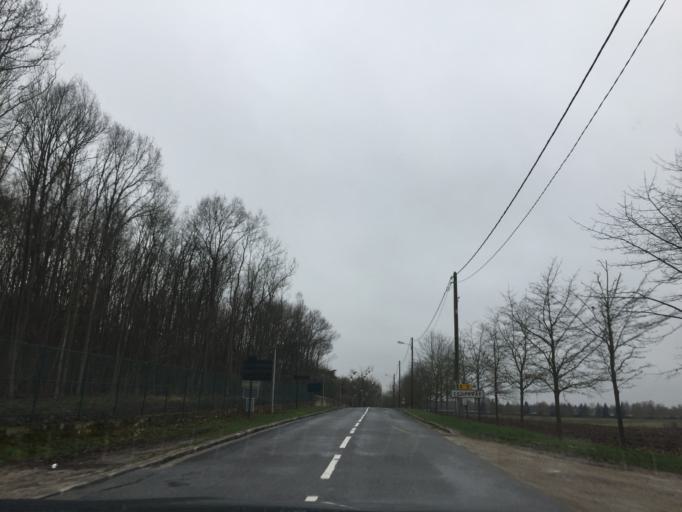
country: FR
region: Ile-de-France
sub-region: Departement de Seine-et-Marne
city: Coupvray
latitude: 48.8853
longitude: 2.7931
